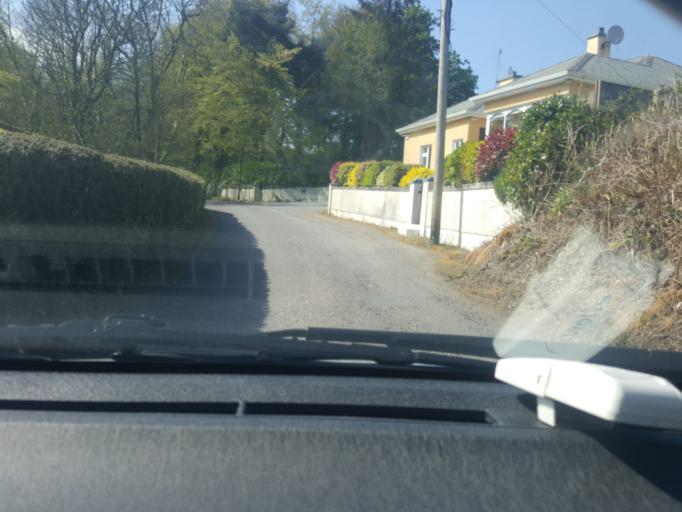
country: IE
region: Munster
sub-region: County Cork
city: Bandon
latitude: 51.7696
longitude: -8.6714
